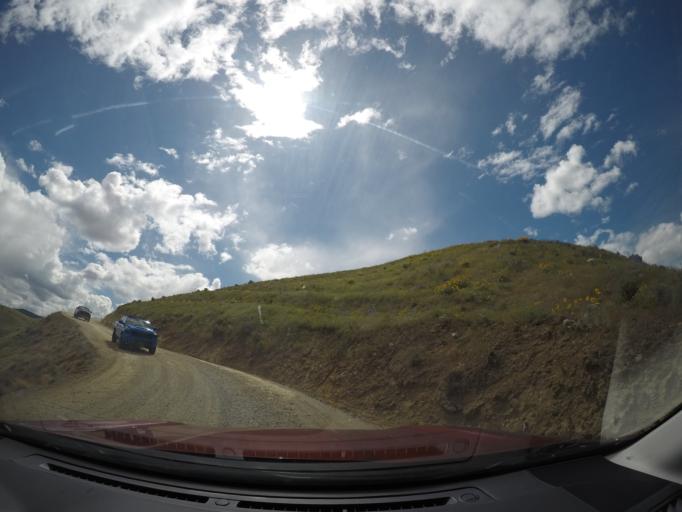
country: US
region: Washington
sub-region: Chelan County
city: West Wenatchee
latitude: 47.4637
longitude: -120.3708
